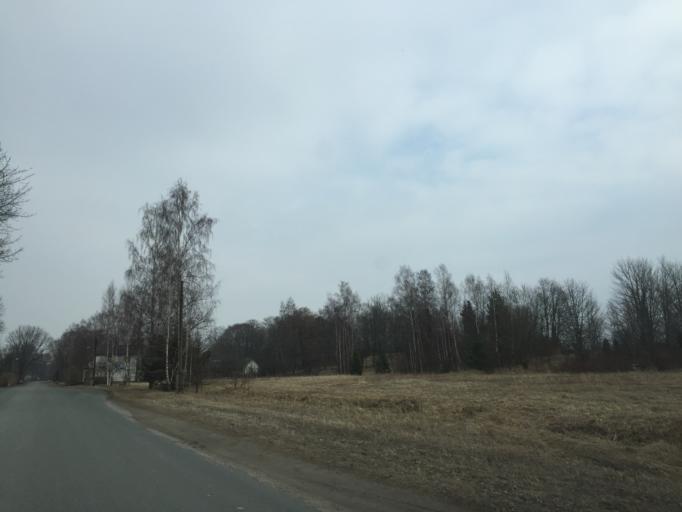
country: LV
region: Salacgrivas
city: Ainazi
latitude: 58.0015
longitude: 24.4374
